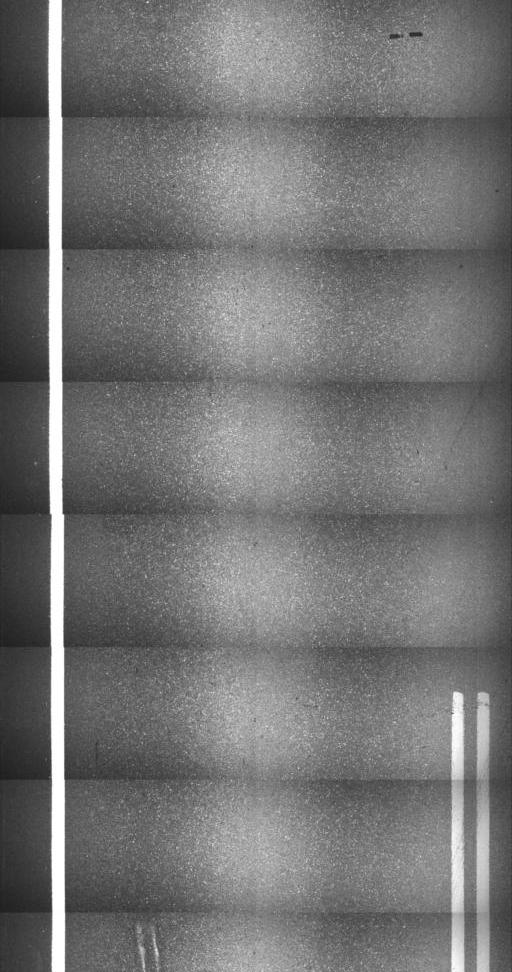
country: US
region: Vermont
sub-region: Washington County
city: Waterbury
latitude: 44.2487
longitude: -72.7861
